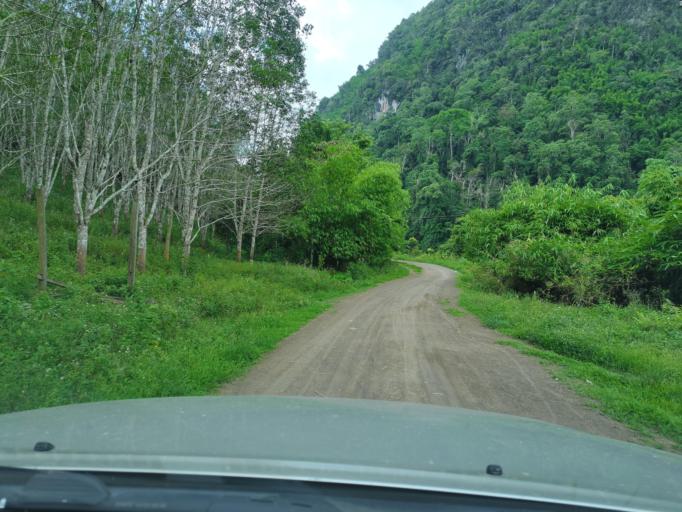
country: LA
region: Loungnamtha
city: Muang Long
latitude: 20.7809
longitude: 101.0165
